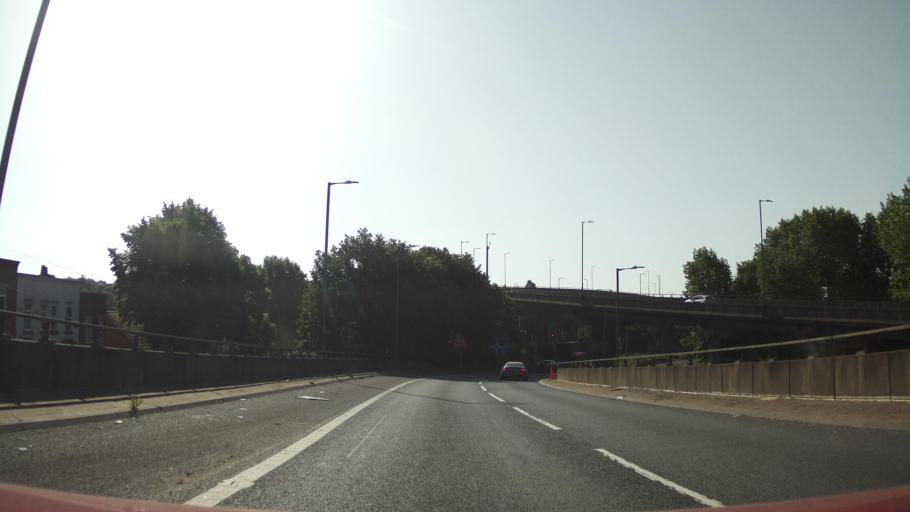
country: GB
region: England
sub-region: City and Borough of Birmingham
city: Birmingham
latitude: 52.5105
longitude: -1.8620
